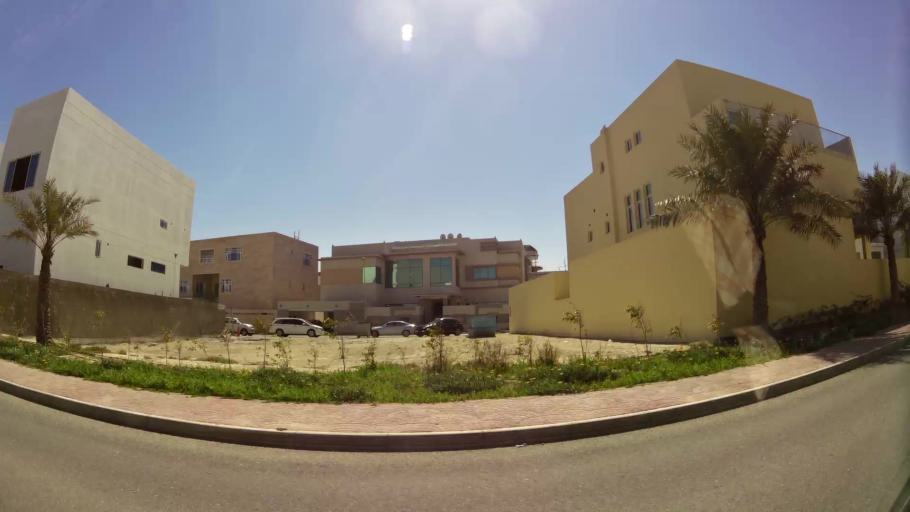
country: BH
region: Muharraq
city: Al Hadd
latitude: 26.2979
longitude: 50.6687
